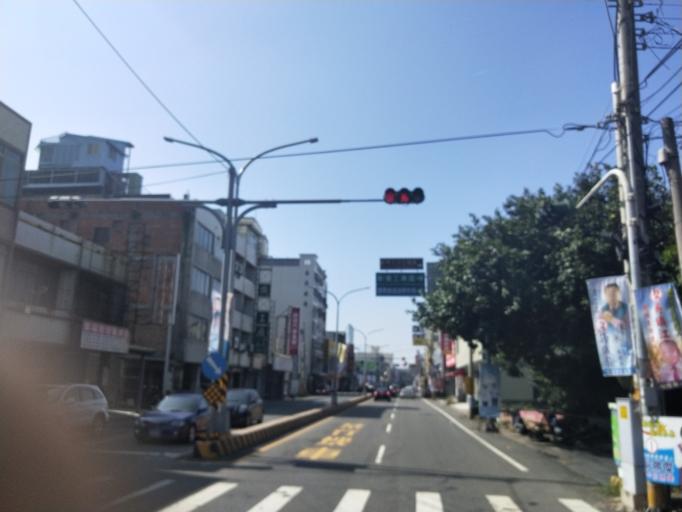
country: TW
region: Taiwan
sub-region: Changhua
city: Chang-hua
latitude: 24.0483
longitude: 120.4438
